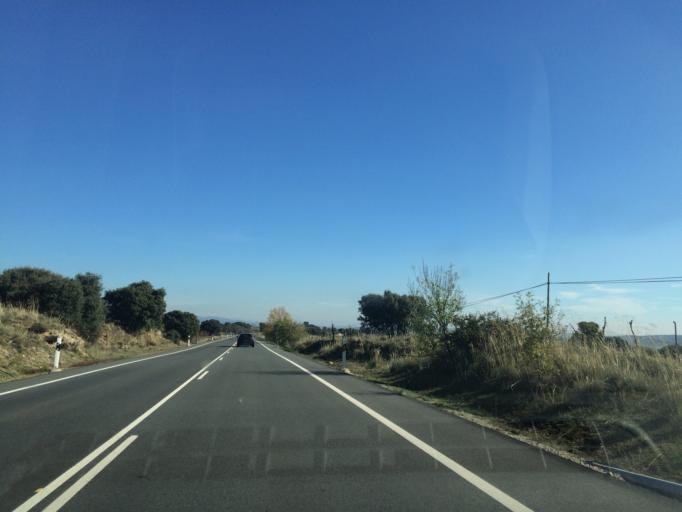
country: ES
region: Madrid
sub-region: Provincia de Madrid
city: Guadalix de la Sierra
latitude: 40.7694
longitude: -3.7340
